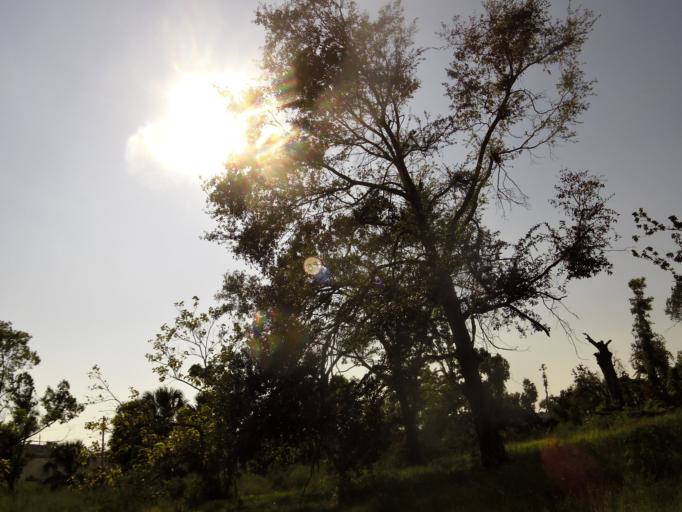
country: US
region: Florida
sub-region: Bay County
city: Panama City
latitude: 30.1594
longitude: -85.6563
